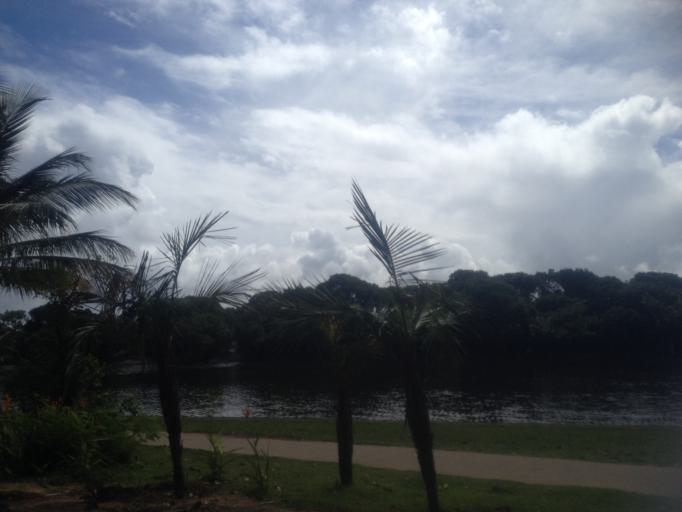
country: BR
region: Bahia
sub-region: Mata De Sao Joao
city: Mata de Sao Joao
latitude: -12.5782
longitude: -38.0126
